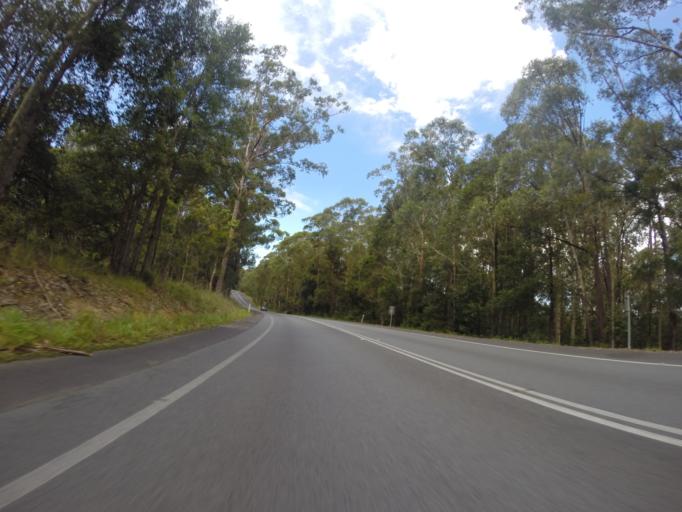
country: AU
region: New South Wales
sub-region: Shoalhaven Shire
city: Falls Creek
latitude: -35.0852
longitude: 150.5384
